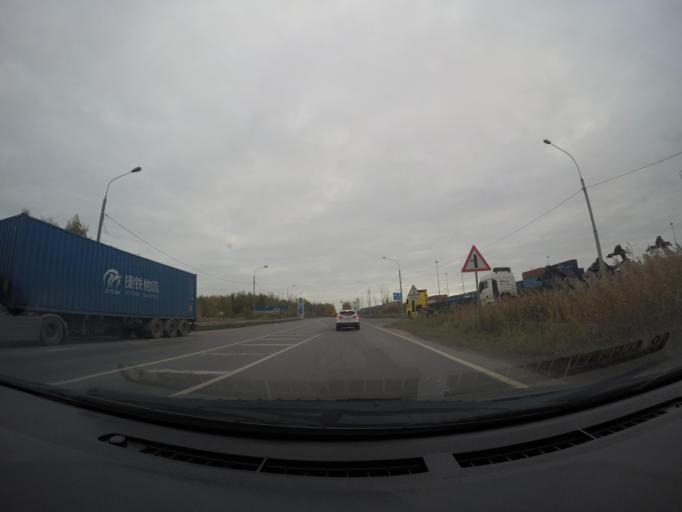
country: RU
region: Moskovskaya
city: Elektrougli
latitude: 55.7254
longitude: 38.2304
